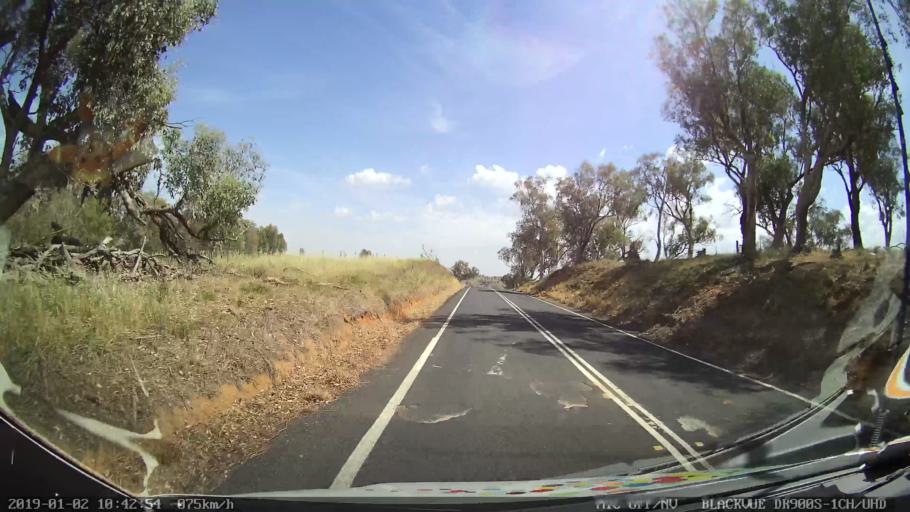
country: AU
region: New South Wales
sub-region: Cootamundra
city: Cootamundra
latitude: -34.7788
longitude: 148.3063
